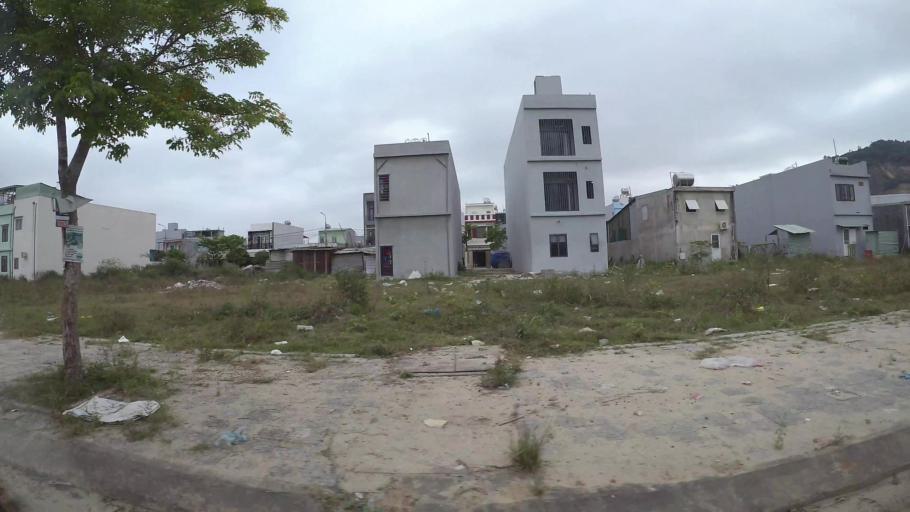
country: VN
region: Da Nang
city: Lien Chieu
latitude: 16.0478
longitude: 108.1642
